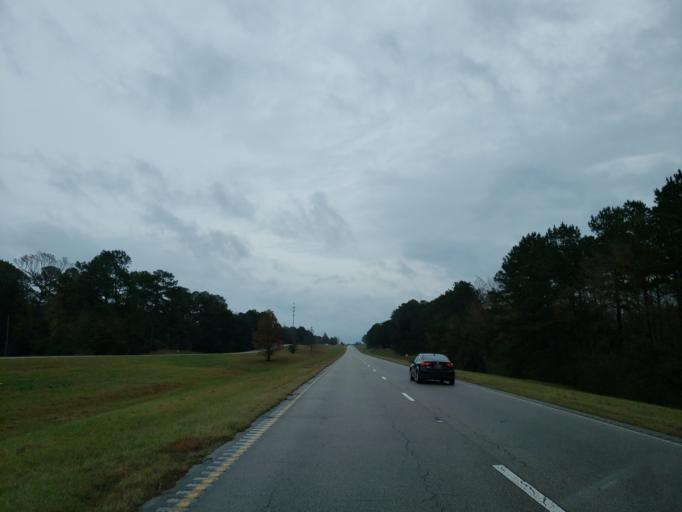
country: US
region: Mississippi
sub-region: Jones County
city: Sharon
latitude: 31.7057
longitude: -88.9334
